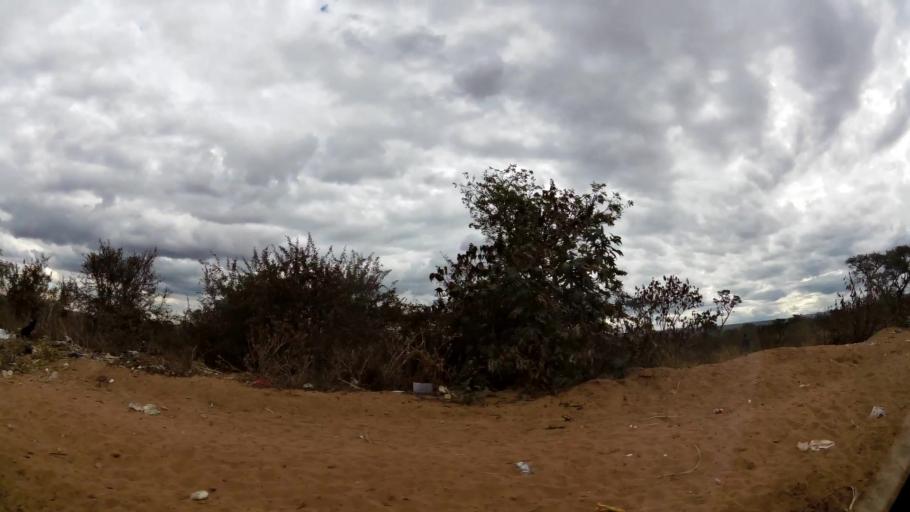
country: ZA
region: Limpopo
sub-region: Waterberg District Municipality
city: Modimolle
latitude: -24.6911
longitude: 28.4204
